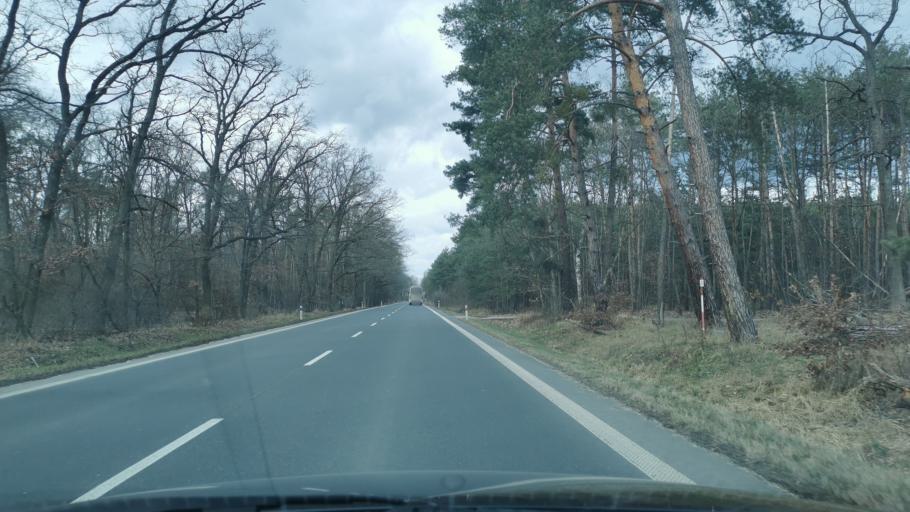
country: CZ
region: South Moravian
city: Tvrdonice
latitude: 48.7167
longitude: 17.0407
